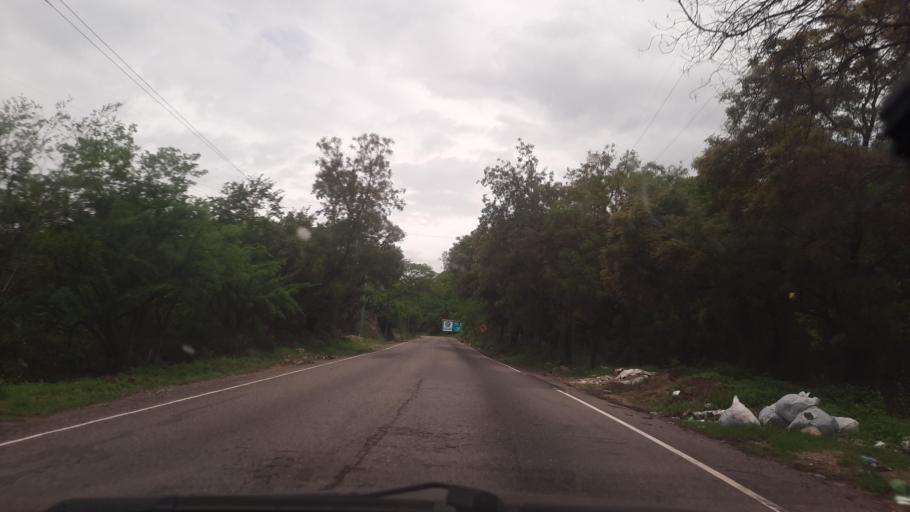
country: GT
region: Zacapa
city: San Jorge
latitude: 14.8882
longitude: -89.5200
